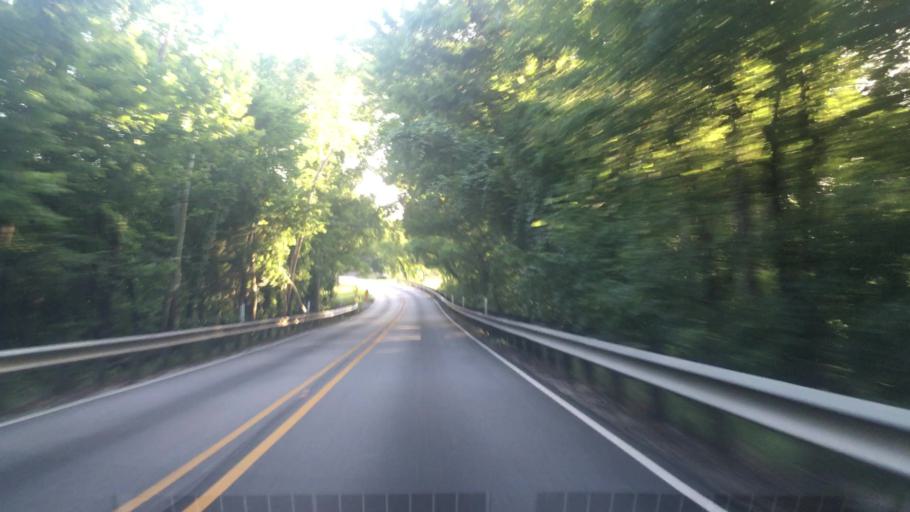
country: US
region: Texas
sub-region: Williamson County
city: Anderson Mill
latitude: 30.4516
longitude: -97.8514
